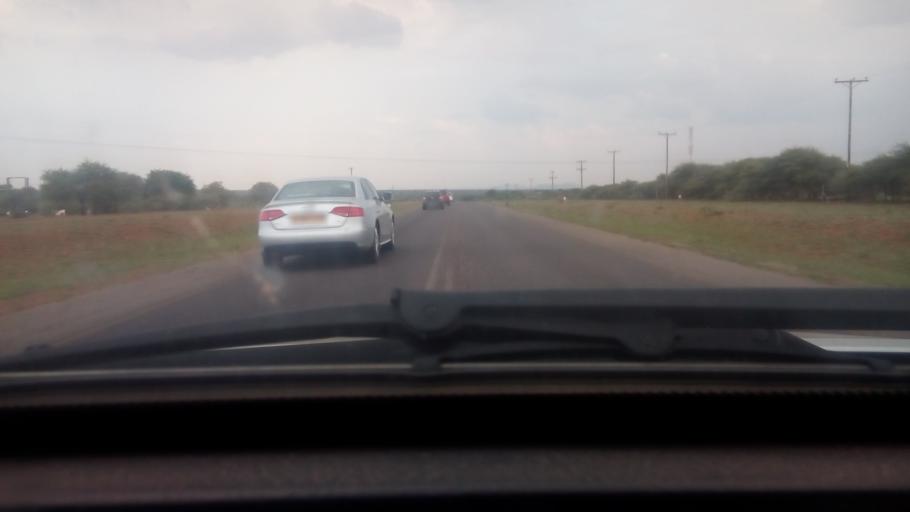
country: BW
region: Kweneng
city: Molepolole
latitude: -24.4603
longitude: 25.6565
